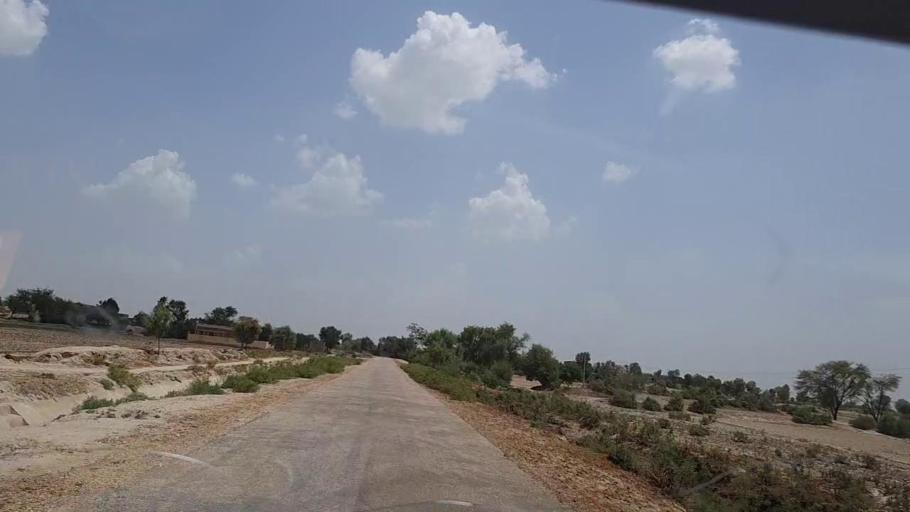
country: PK
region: Sindh
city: Bhan
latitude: 26.5157
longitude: 67.6394
